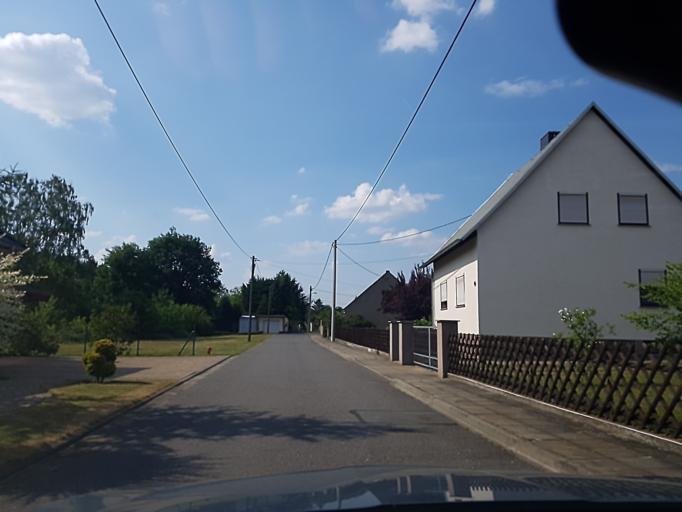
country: DE
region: Brandenburg
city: Schonborn
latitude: 51.5389
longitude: 13.4649
